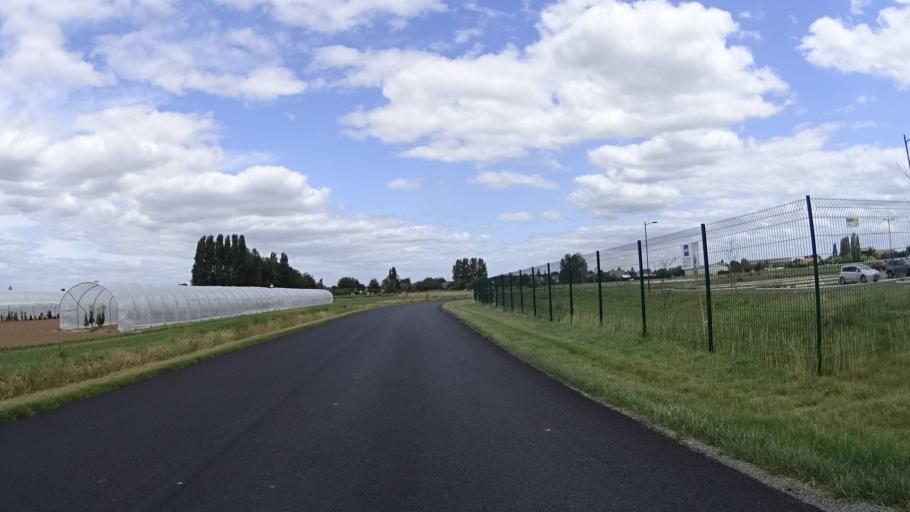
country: FR
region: Pays de la Loire
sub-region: Departement de Maine-et-Loire
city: La Menitre
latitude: 47.4053
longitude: -0.2784
